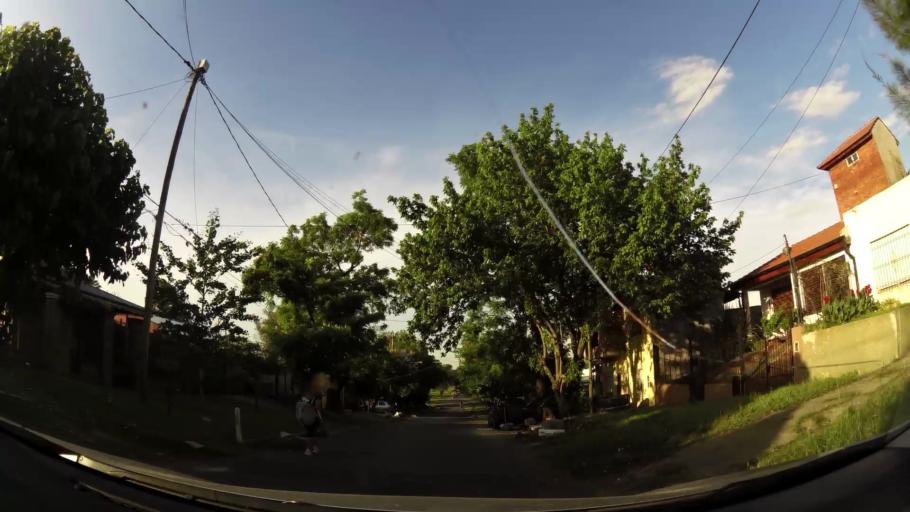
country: AR
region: Buenos Aires
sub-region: Partido de Tigre
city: Tigre
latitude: -34.4515
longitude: -58.6333
